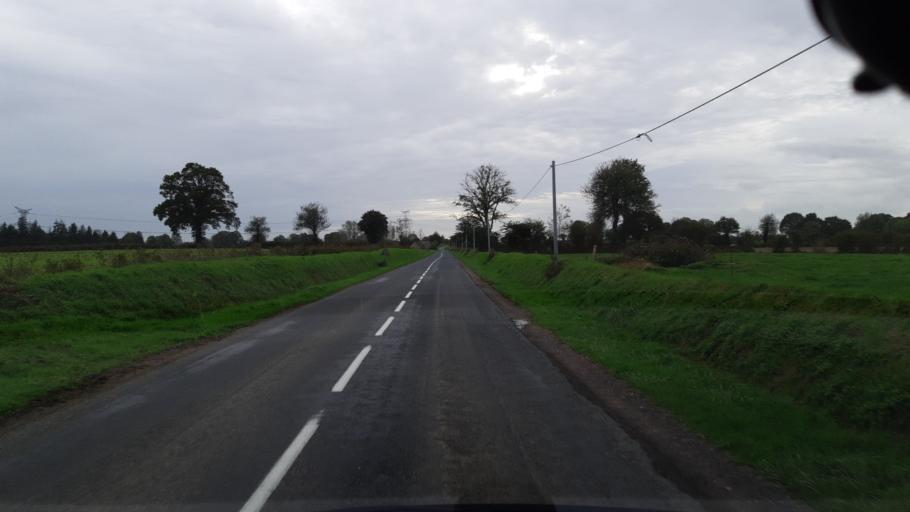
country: FR
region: Lower Normandy
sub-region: Departement de la Manche
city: Hambye
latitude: 48.9885
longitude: -1.2071
